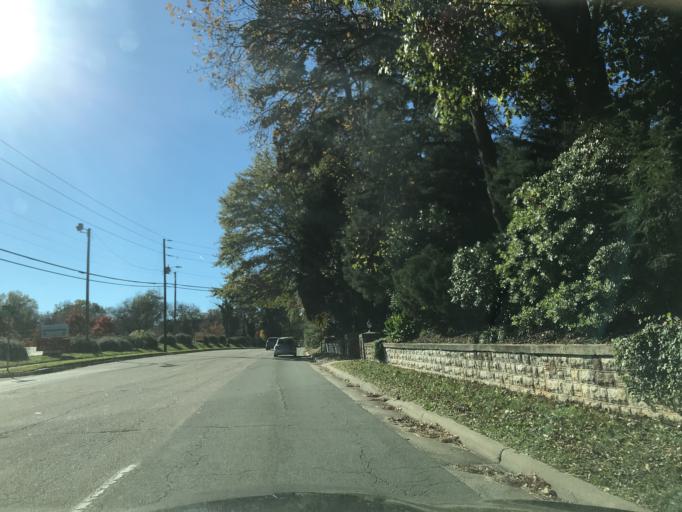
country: US
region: North Carolina
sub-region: Wake County
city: Raleigh
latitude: 35.7989
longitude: -78.6268
